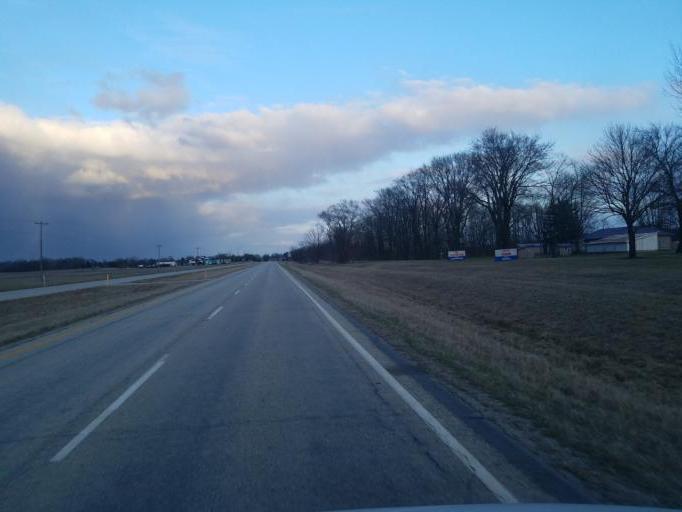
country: US
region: Indiana
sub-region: Henry County
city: Knightstown
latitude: 39.8021
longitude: -85.4530
